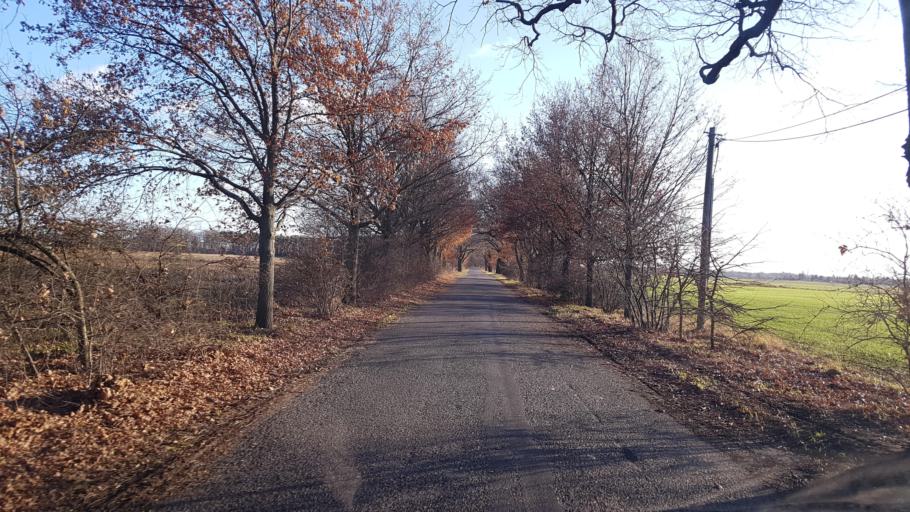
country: DE
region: Brandenburg
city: Forst
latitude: 51.7677
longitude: 14.6038
